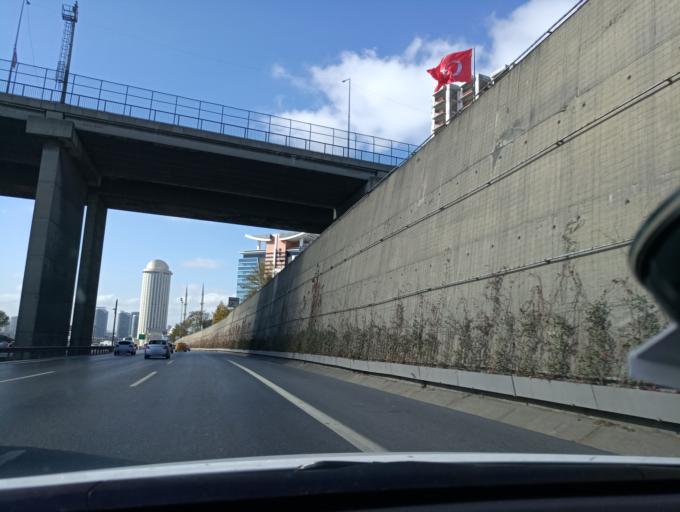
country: TR
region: Istanbul
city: Mahmutbey
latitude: 41.0644
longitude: 28.8336
